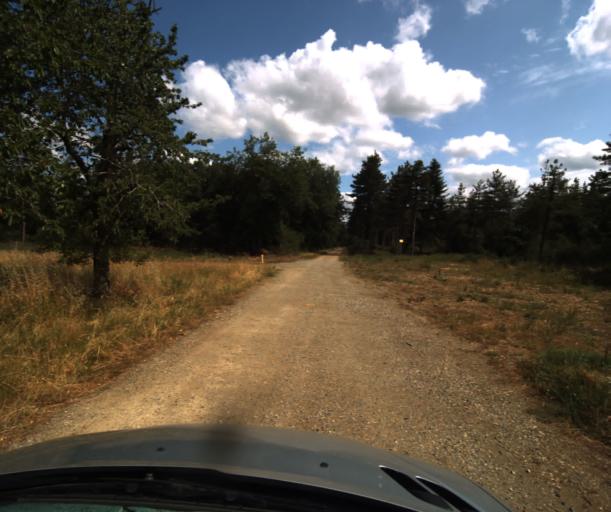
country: FR
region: Midi-Pyrenees
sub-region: Departement du Tarn-et-Garonne
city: Montech
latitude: 43.9260
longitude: 1.2739
